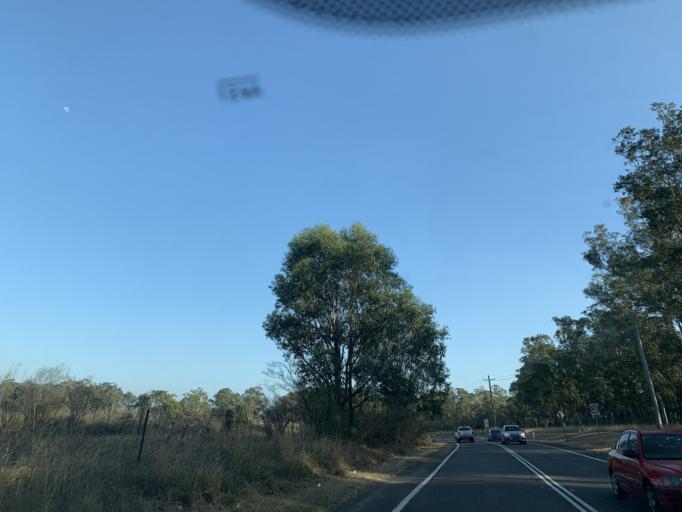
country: AU
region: New South Wales
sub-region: Fairfield
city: Horsley Park
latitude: -33.8327
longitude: 150.8737
